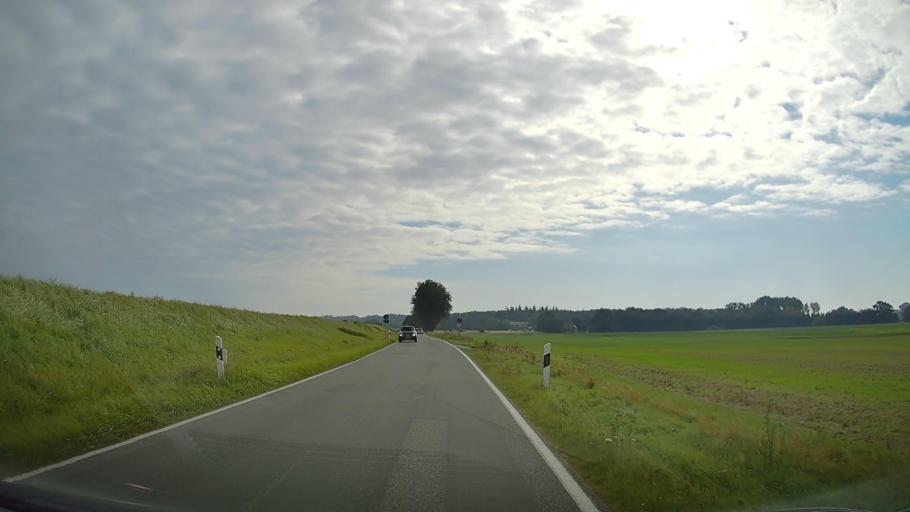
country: DE
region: Schleswig-Holstein
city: Blekendorf
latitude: 54.3310
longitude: 10.6494
